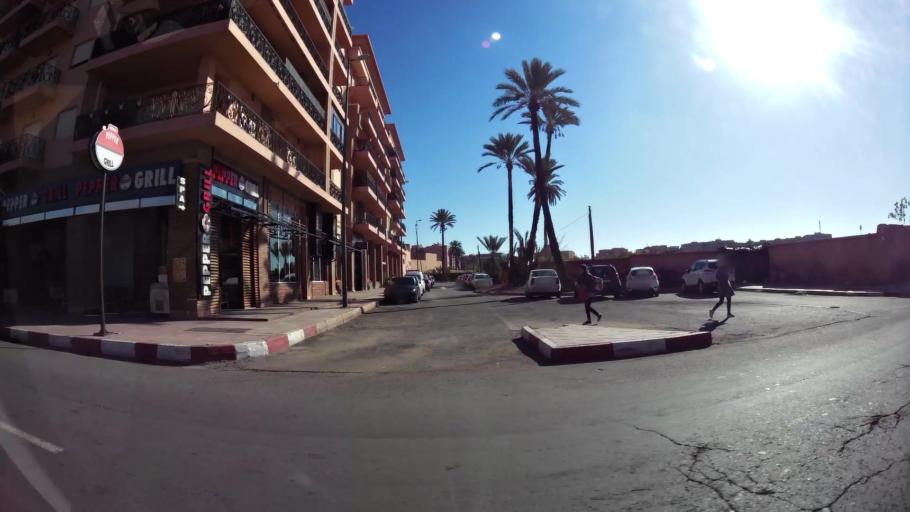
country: MA
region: Marrakech-Tensift-Al Haouz
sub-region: Marrakech
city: Marrakesh
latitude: 31.6387
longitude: -8.0038
